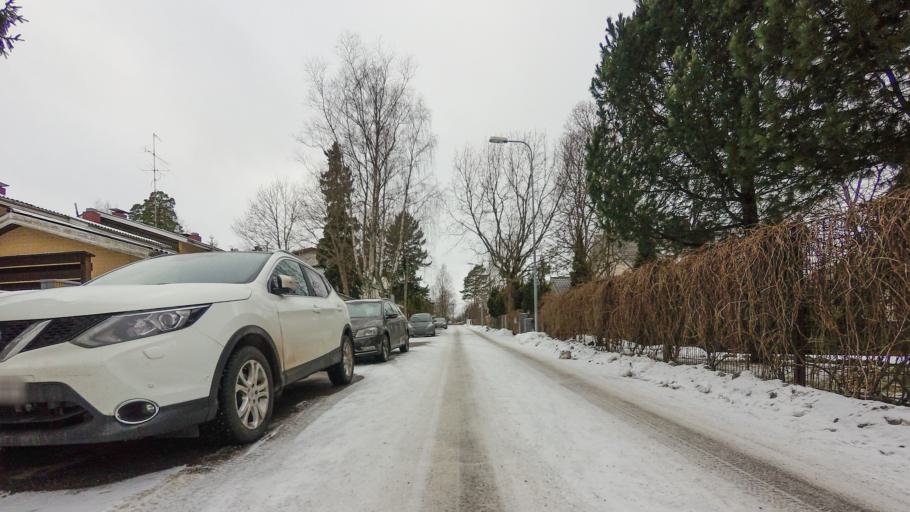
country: FI
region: Uusimaa
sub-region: Helsinki
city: Vantaa
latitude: 60.1913
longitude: 25.0536
